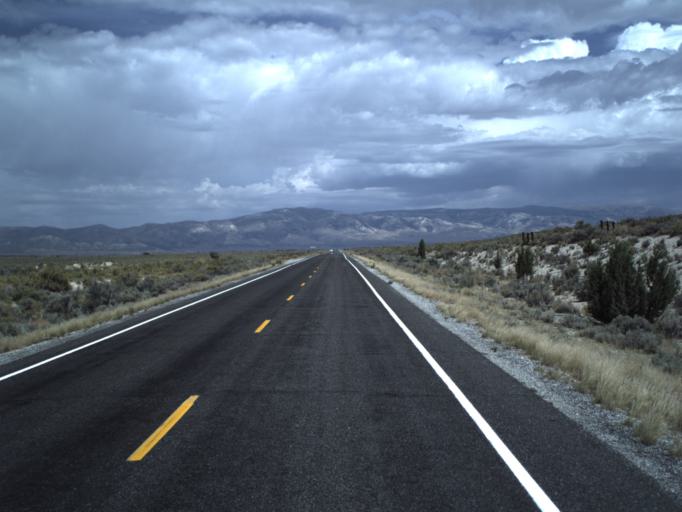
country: US
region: Idaho
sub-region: Cassia County
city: Burley
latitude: 41.6833
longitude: -113.5398
